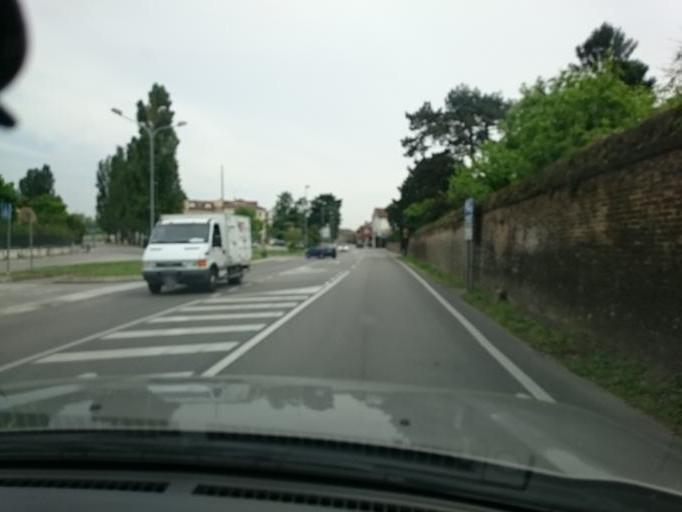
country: IT
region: Veneto
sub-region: Provincia di Padova
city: Noventa
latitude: 45.4149
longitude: 11.9563
